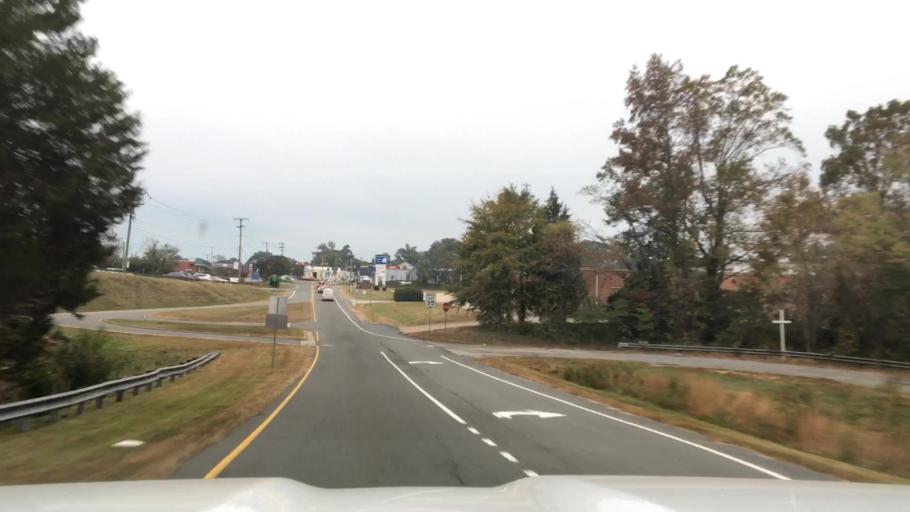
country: US
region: Virginia
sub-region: Hanover County
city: Mechanicsville
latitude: 37.6053
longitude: -77.3687
